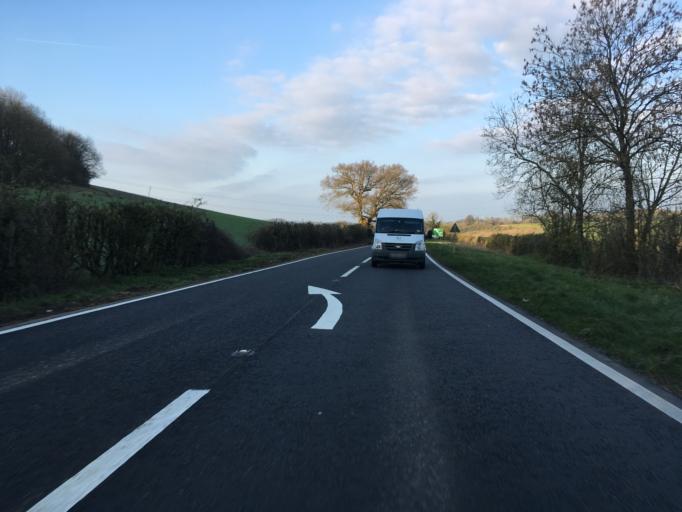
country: GB
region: England
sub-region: Gloucestershire
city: Charlton Kings
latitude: 51.8565
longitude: -2.0411
